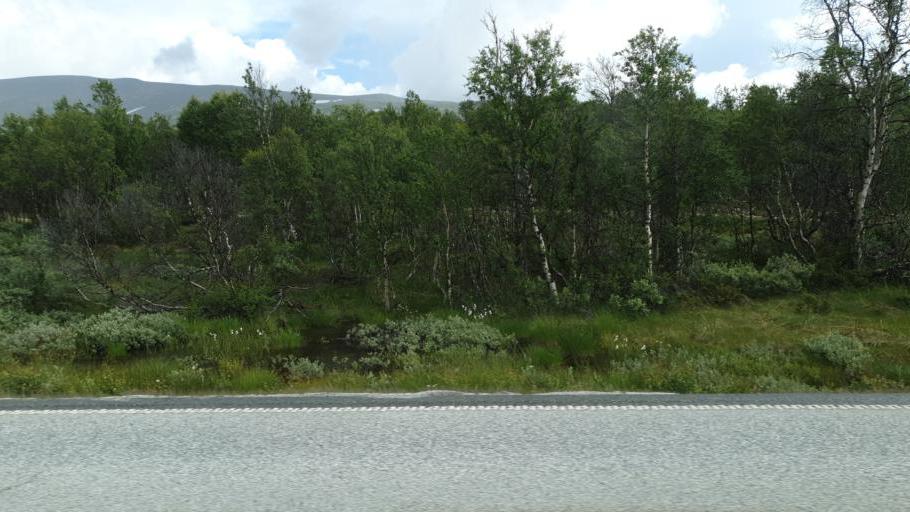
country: NO
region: Oppland
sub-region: Dovre
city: Dovre
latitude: 62.1354
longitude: 9.3147
